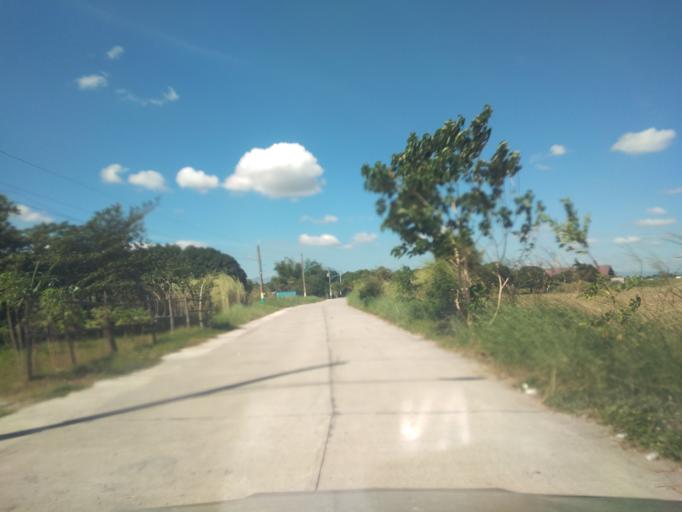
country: PH
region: Central Luzon
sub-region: Province of Pampanga
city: Santa Rita
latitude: 15.0308
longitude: 120.6268
